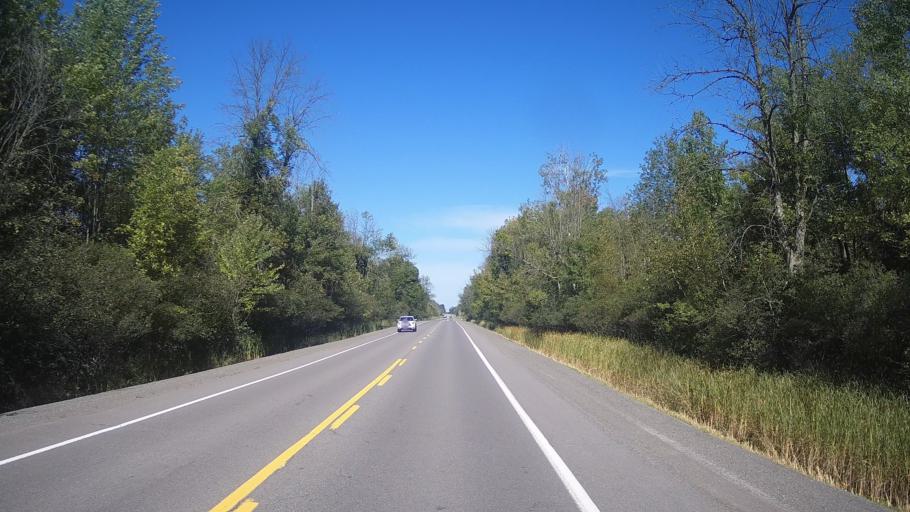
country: CA
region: Ontario
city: Bells Corners
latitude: 45.0798
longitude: -75.6512
